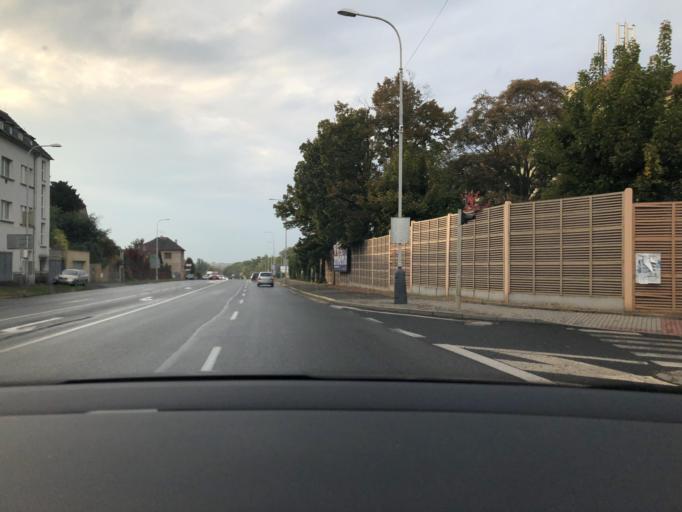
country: CZ
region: Central Bohemia
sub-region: Okres Kolin
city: Kolin
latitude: 50.0306
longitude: 15.1890
